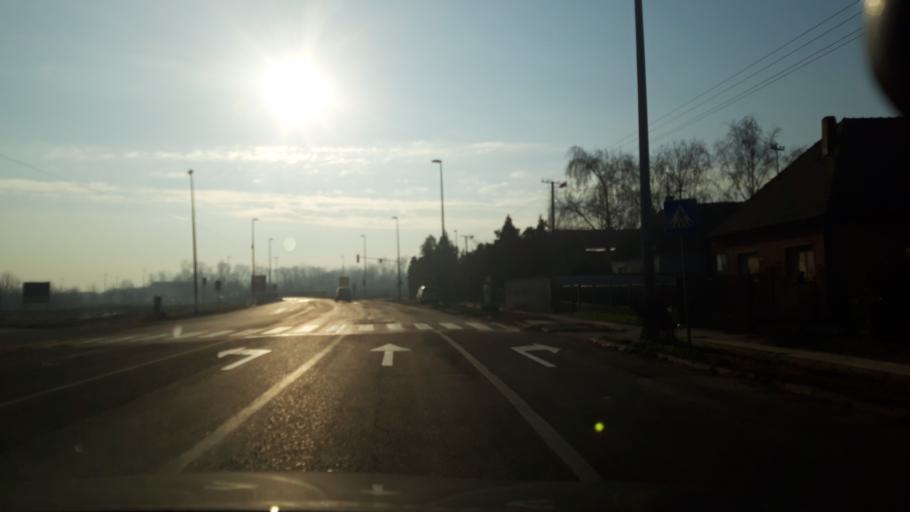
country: RS
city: Pocerski Pricinovic
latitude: 44.7417
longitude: 19.7222
